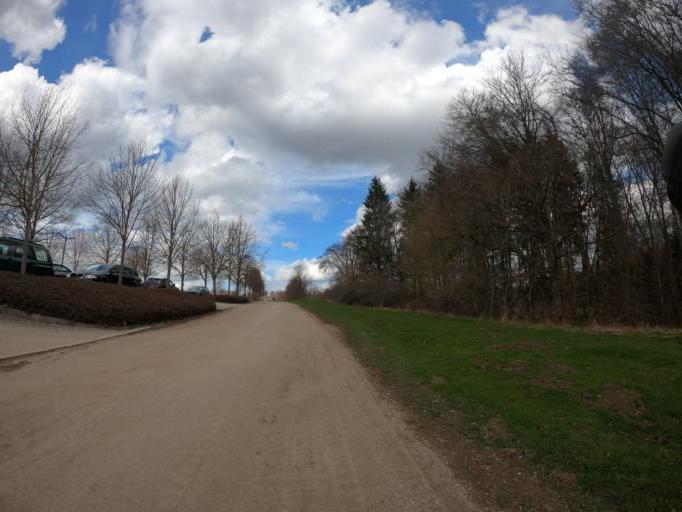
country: DE
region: Baden-Wuerttemberg
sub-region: Tuebingen Region
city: Pfullingen
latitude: 48.3867
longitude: 9.2193
